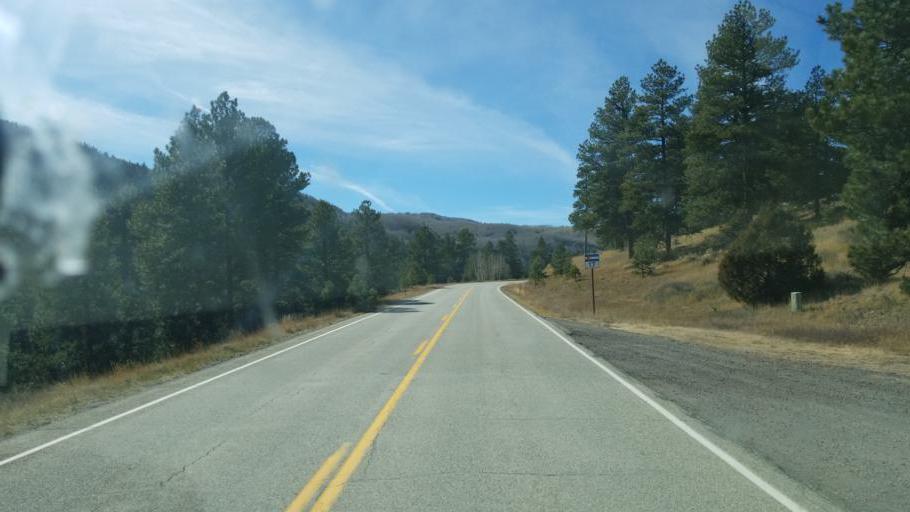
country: US
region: Colorado
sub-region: Conejos County
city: Conejos
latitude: 37.0740
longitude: -106.2756
